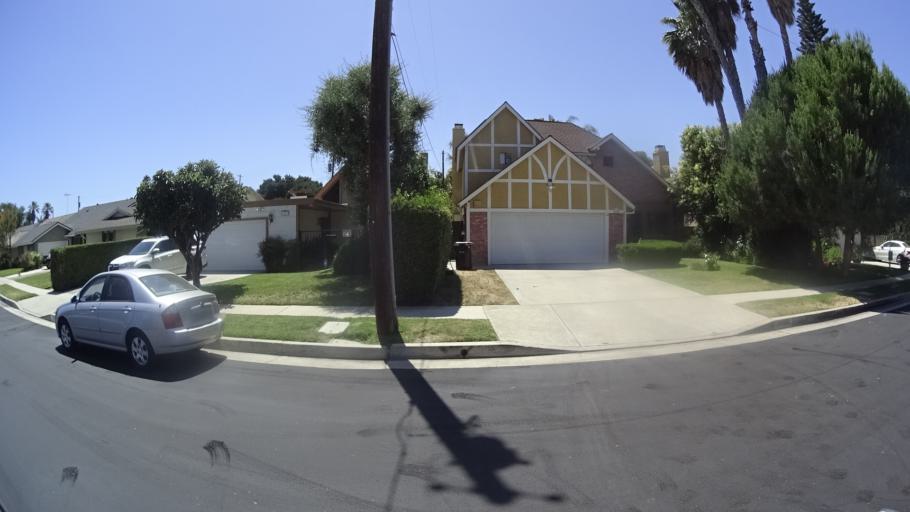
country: US
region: California
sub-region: Los Angeles County
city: Northridge
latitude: 34.1905
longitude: -118.5110
